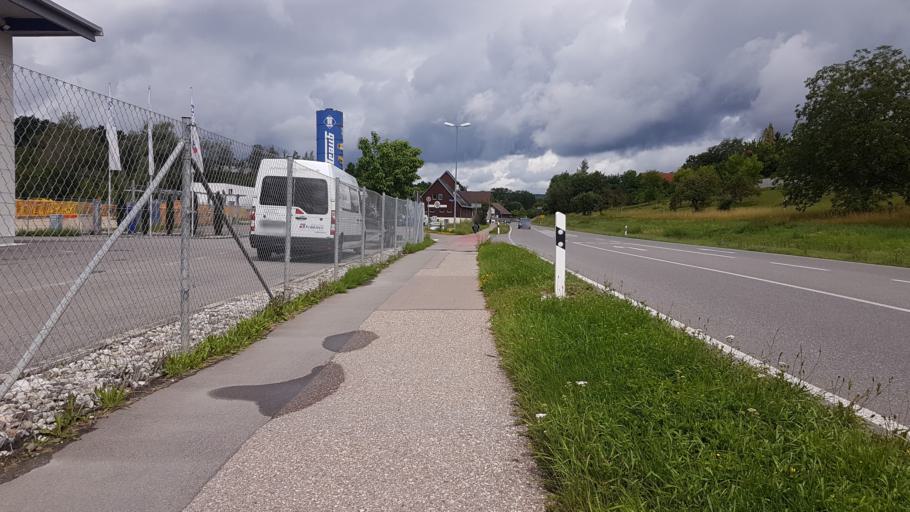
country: DE
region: Baden-Wuerttemberg
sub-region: Tuebingen Region
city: Ehingen
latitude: 48.2765
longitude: 9.7187
